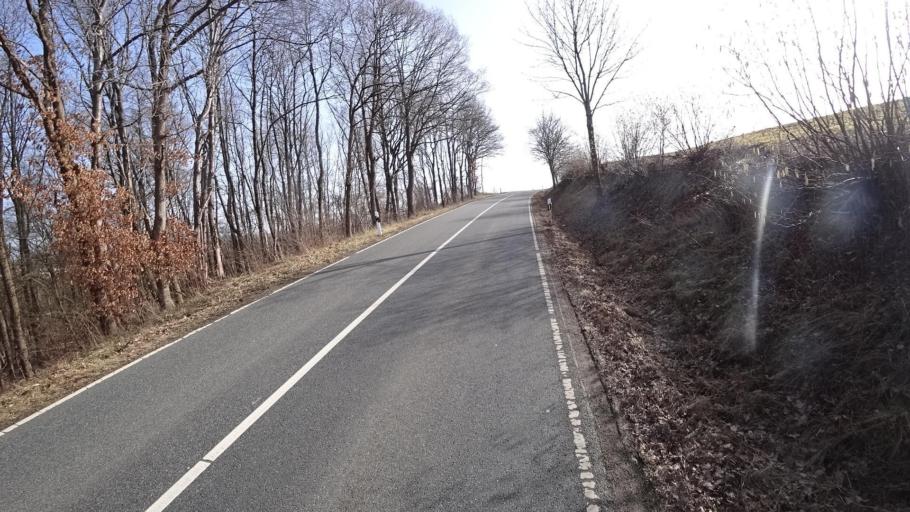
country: DE
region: Rheinland-Pfalz
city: Etzbach
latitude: 50.7730
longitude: 7.6970
